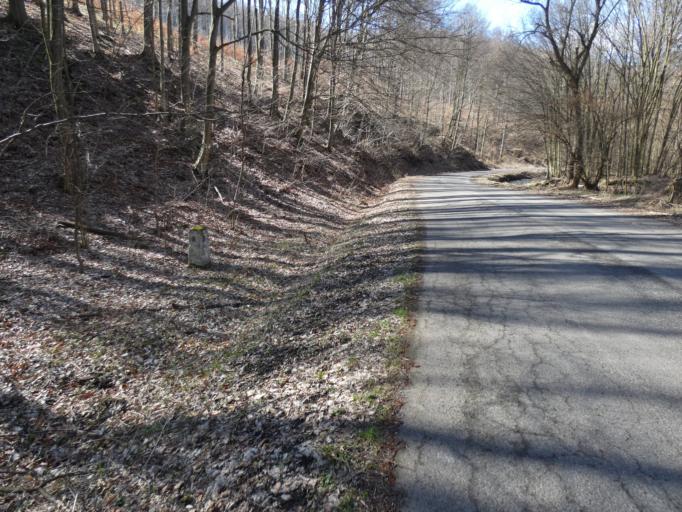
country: HU
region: Nograd
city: Diosjeno
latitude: 47.9830
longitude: 18.9797
